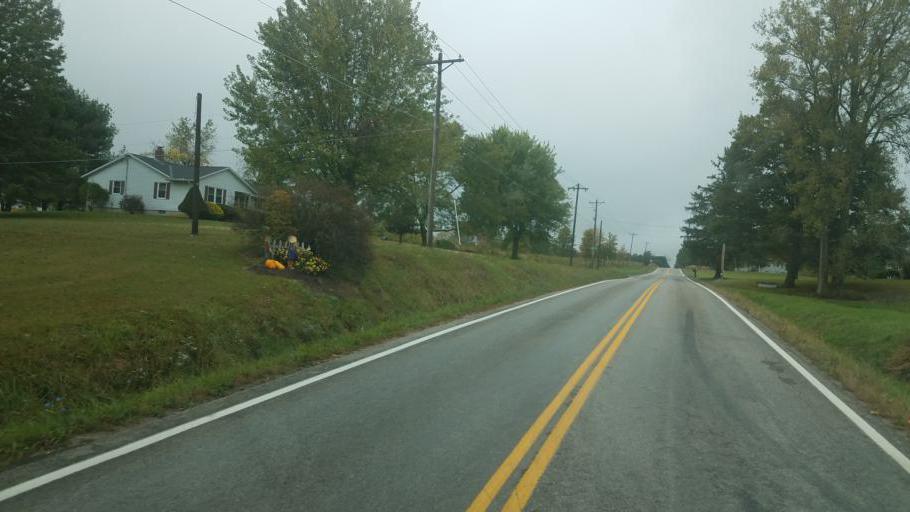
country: US
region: Ohio
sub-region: Ashland County
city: Ashland
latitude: 40.7988
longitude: -82.3397
